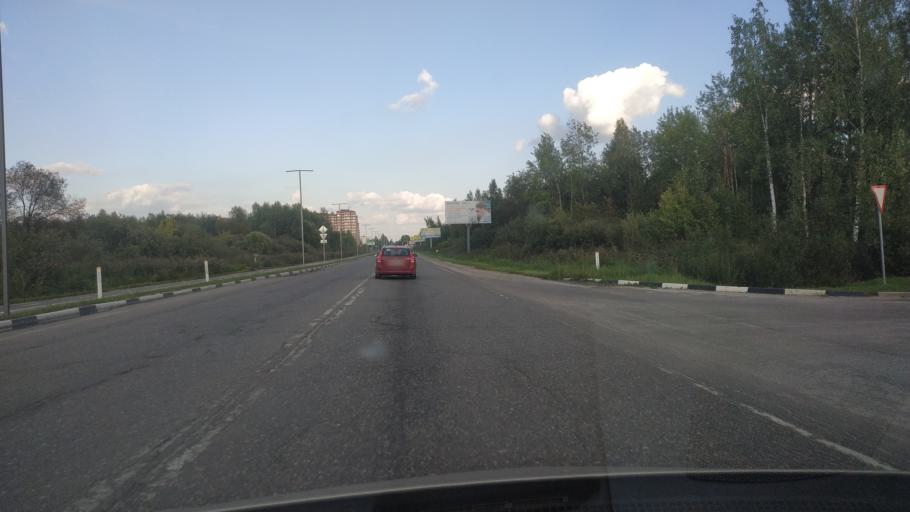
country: RU
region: Moskovskaya
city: Shatura
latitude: 55.5757
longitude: 39.5031
